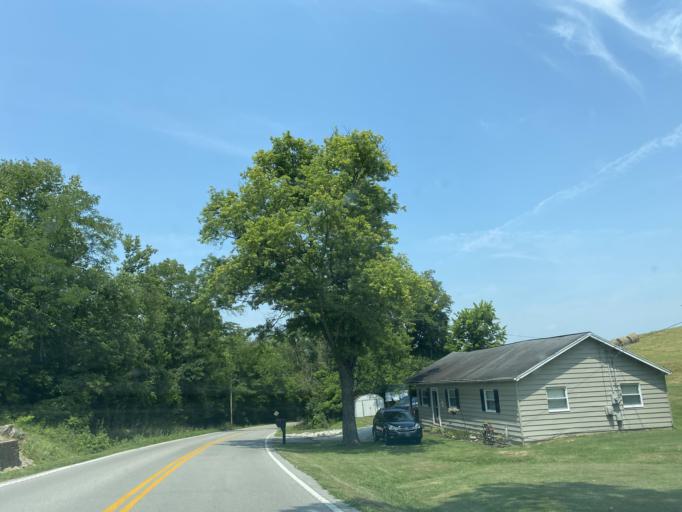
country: US
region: Kentucky
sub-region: Kenton County
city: Ryland Heights
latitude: 38.9078
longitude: -84.4492
